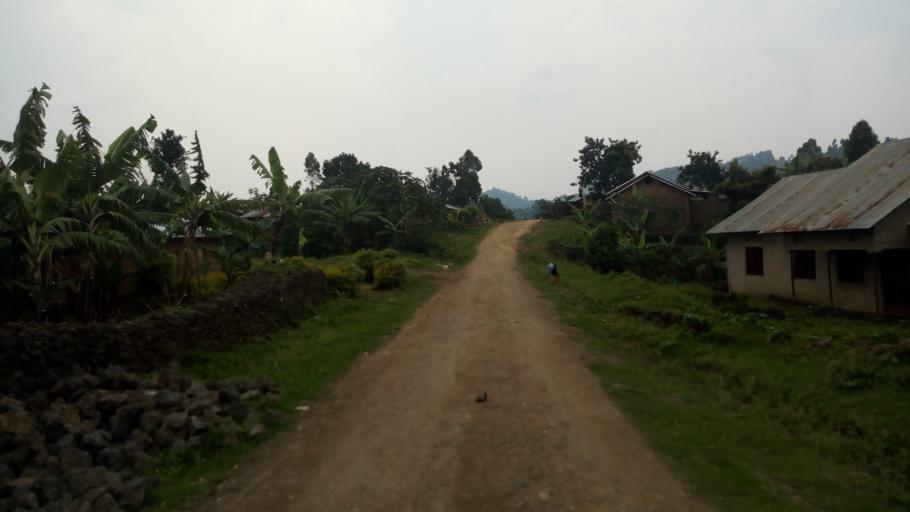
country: UG
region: Western Region
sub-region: Kisoro District
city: Kisoro
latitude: -1.2668
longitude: 29.6259
